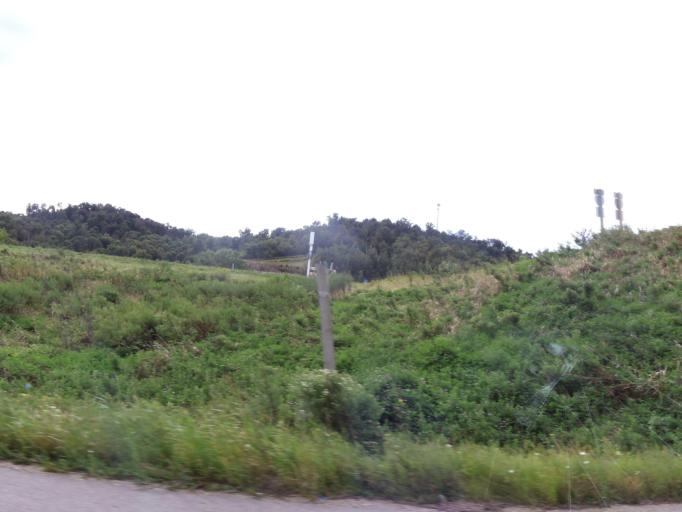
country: US
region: Wisconsin
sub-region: La Crosse County
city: West Salem
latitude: 43.8918
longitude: -91.0750
